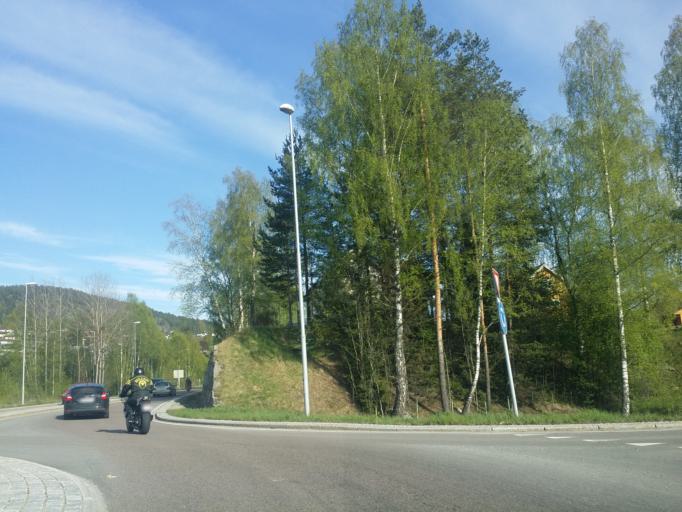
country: NO
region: Telemark
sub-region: Notodden
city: Notodden
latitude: 59.5762
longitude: 9.1901
